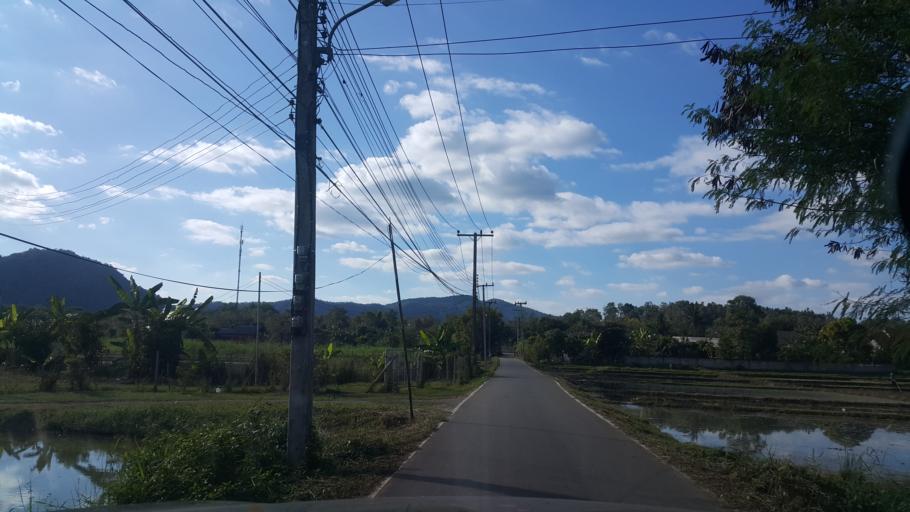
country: TH
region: Chiang Mai
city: Mae On
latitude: 18.7892
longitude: 99.2565
